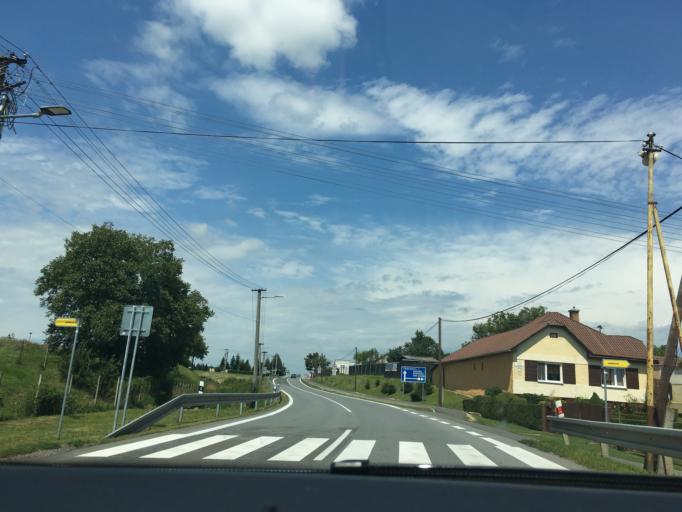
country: SK
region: Presovsky
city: Vranov nad Topl'ou
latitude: 48.8223
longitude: 21.6902
